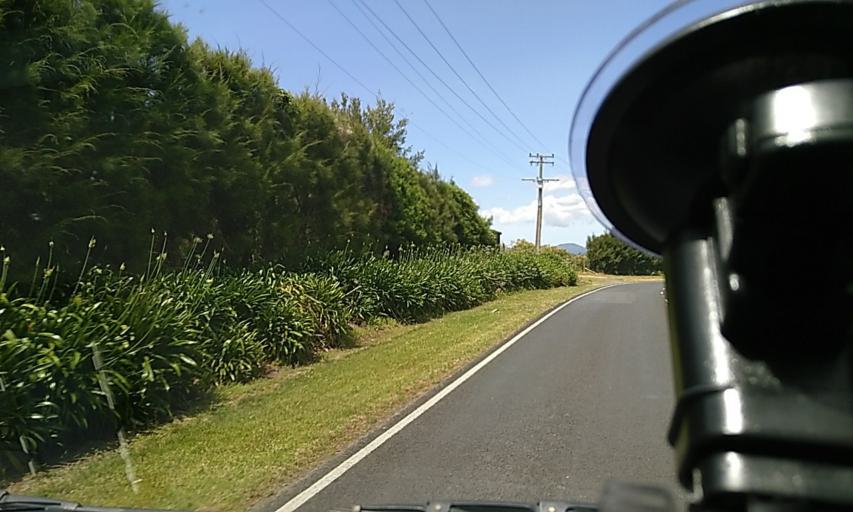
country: NZ
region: Bay of Plenty
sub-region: Western Bay of Plenty District
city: Waihi Beach
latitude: -37.4546
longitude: 175.9414
